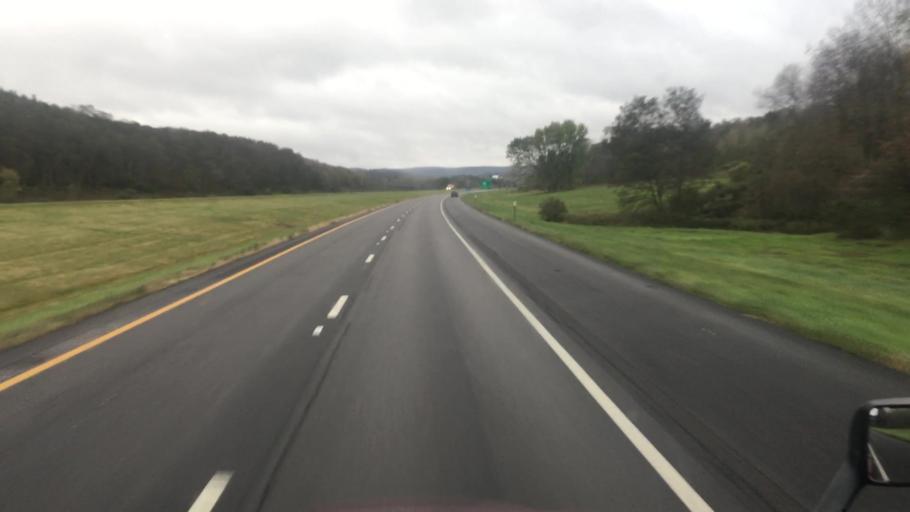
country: US
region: New York
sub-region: Otsego County
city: Unadilla
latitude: 42.3395
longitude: -75.2723
